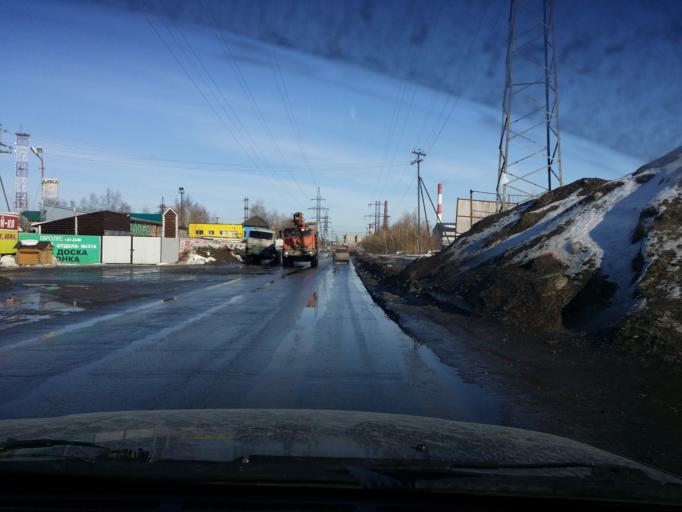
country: RU
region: Khanty-Mansiyskiy Avtonomnyy Okrug
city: Nizhnevartovsk
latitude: 60.9329
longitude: 76.5245
